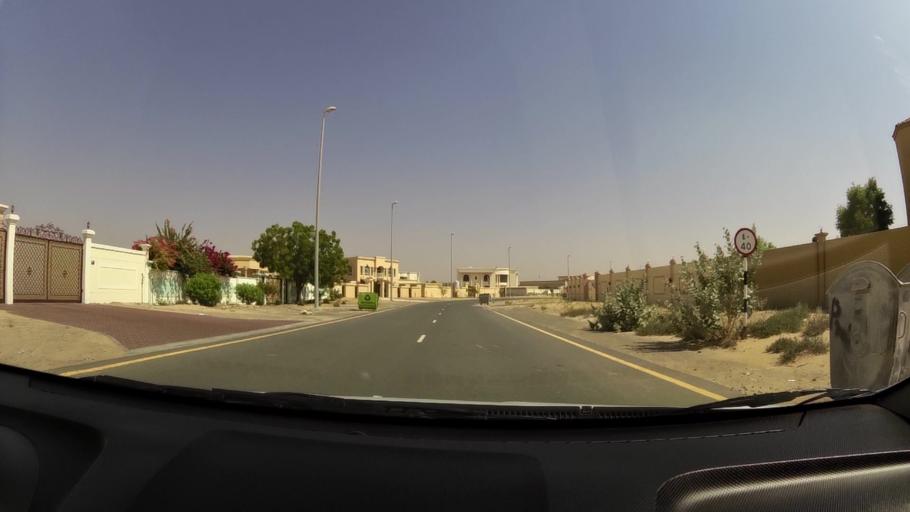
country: AE
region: Umm al Qaywayn
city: Umm al Qaywayn
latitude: 25.4913
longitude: 55.6041
